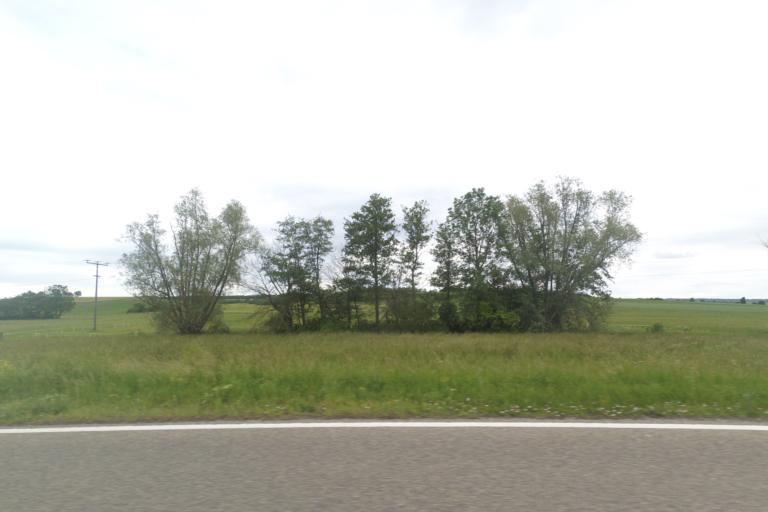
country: DE
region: Bavaria
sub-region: Regierungsbezirk Mittelfranken
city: Sugenheim
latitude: 49.5826
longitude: 10.4115
